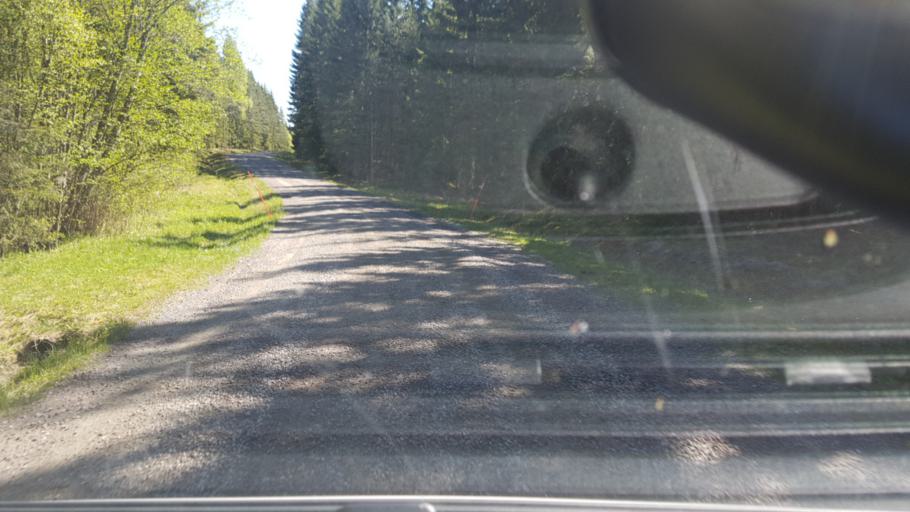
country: SE
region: Vaermland
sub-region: Eda Kommun
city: Charlottenberg
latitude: 59.9021
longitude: 12.3797
